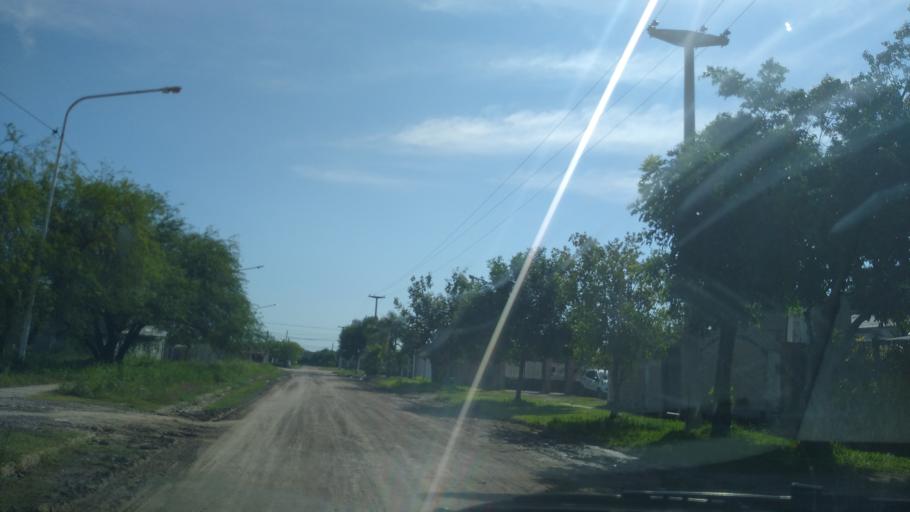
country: AR
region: Chaco
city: Barranqueras
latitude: -27.4940
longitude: -58.9595
